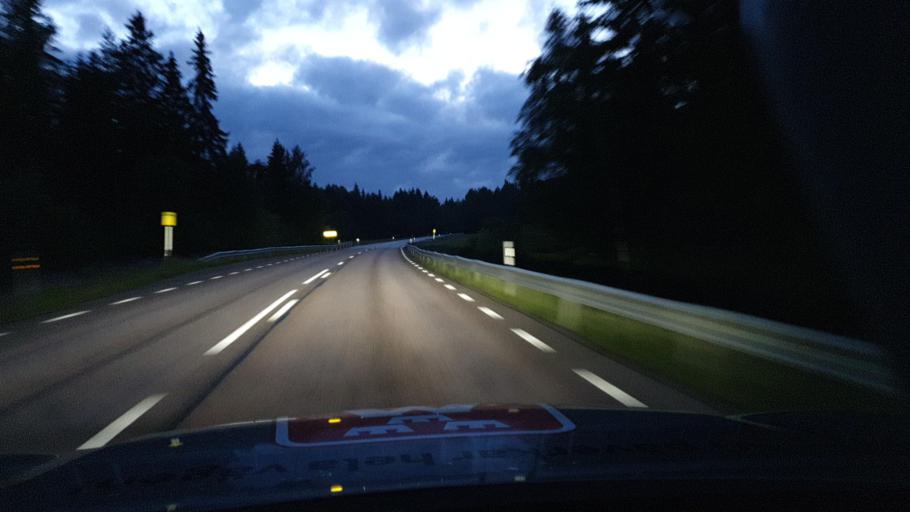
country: SE
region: Vaermland
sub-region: Storfors Kommun
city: Storfors
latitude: 59.4712
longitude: 14.3307
